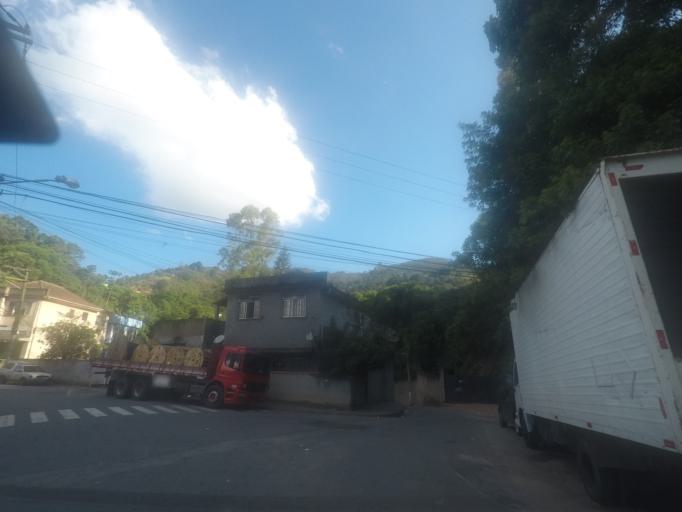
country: BR
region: Rio de Janeiro
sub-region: Petropolis
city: Petropolis
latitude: -22.5055
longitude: -43.1544
